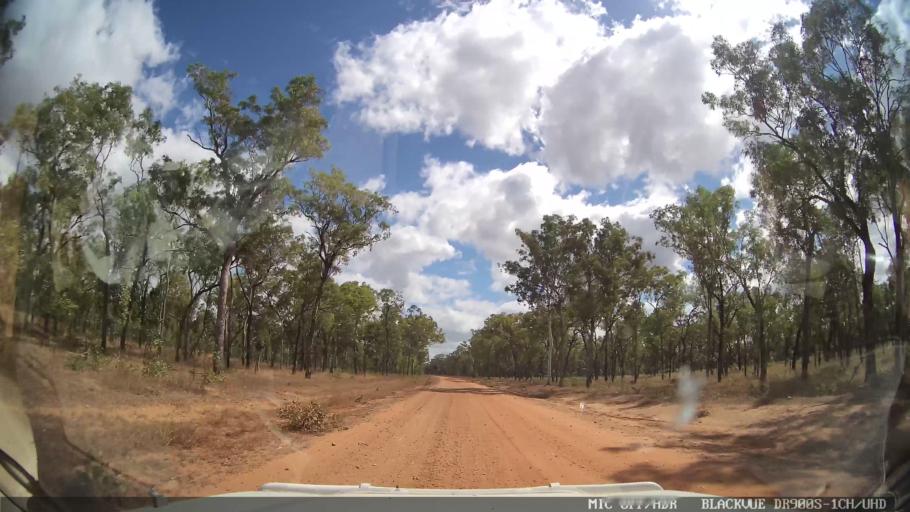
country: AU
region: Queensland
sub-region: Cook
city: Cooktown
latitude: -15.3515
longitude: 144.4665
